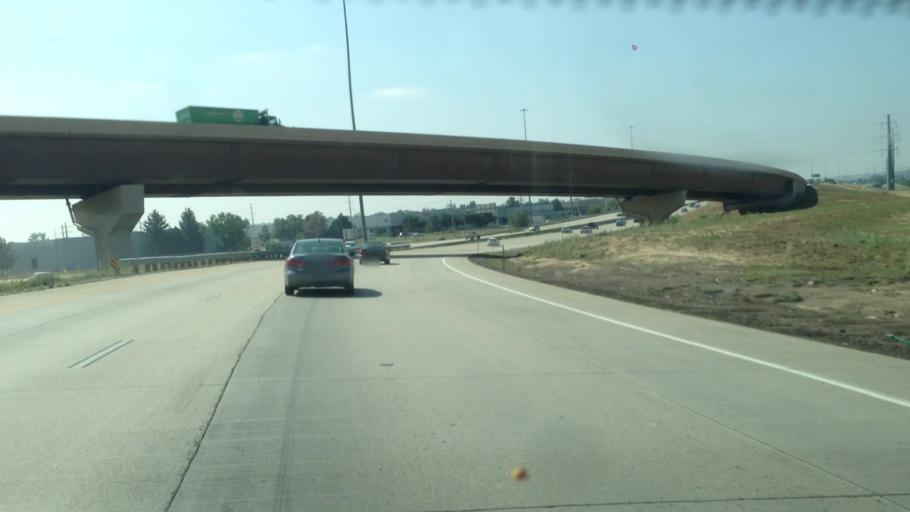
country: US
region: Colorado
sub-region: Adams County
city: Aurora
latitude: 39.7710
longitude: -104.8287
